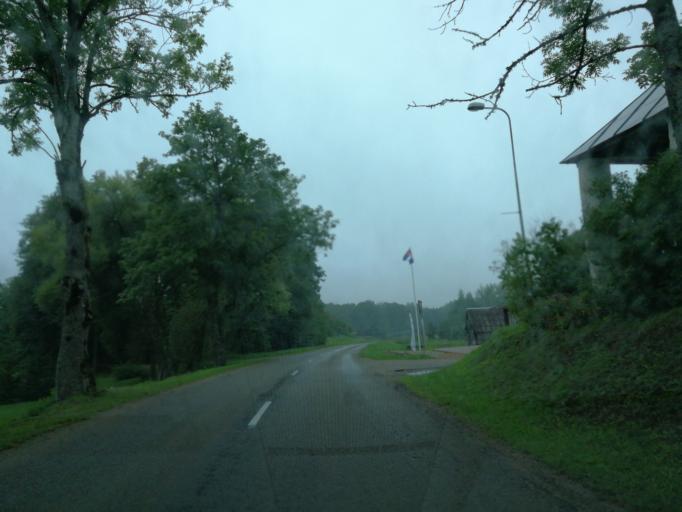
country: LV
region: Preilu Rajons
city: Jaunaglona
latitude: 56.2693
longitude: 27.0378
